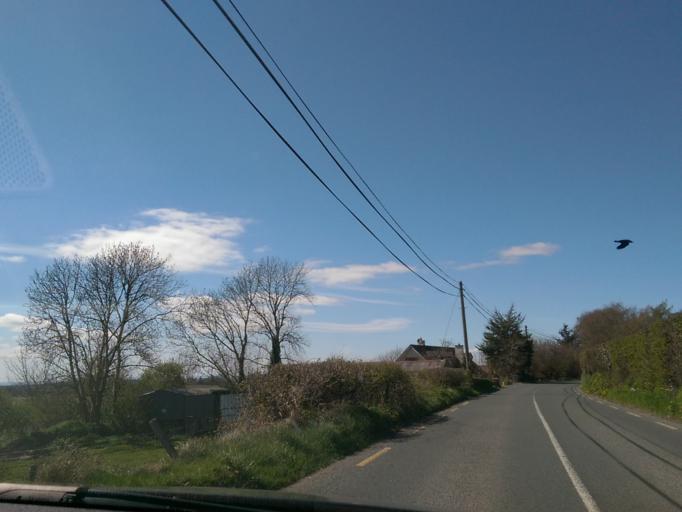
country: IE
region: Leinster
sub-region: Wicklow
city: Baltinglass
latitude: 52.8774
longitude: -6.5808
